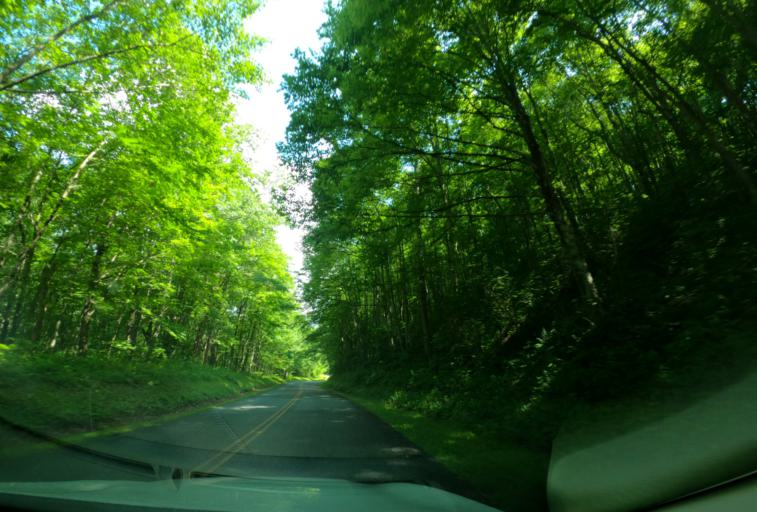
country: US
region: North Carolina
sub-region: Haywood County
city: Hazelwood
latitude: 35.4381
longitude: -83.0798
